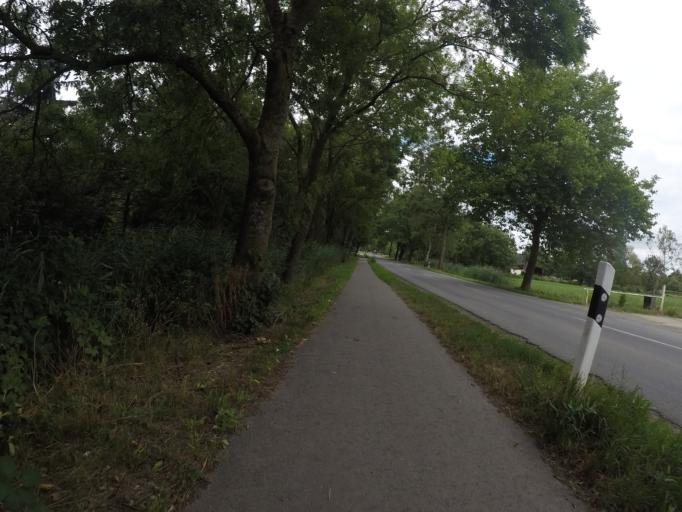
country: DE
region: Lower Saxony
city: Grossenworden
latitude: 53.6670
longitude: 9.2965
